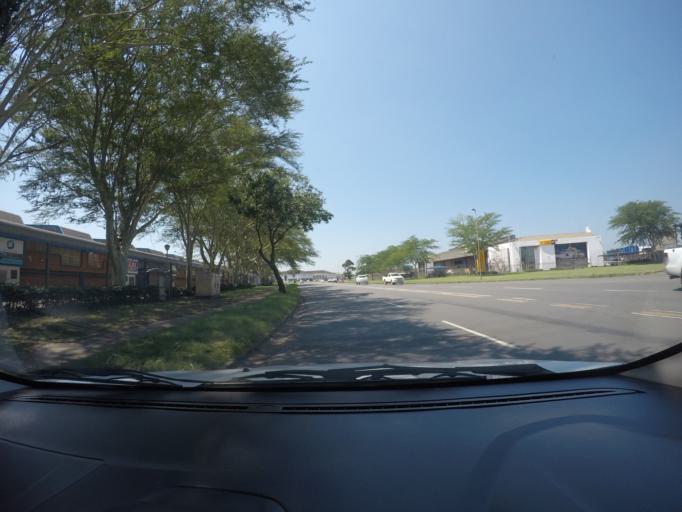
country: ZA
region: KwaZulu-Natal
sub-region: uThungulu District Municipality
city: Richards Bay
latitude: -28.7561
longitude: 32.0255
